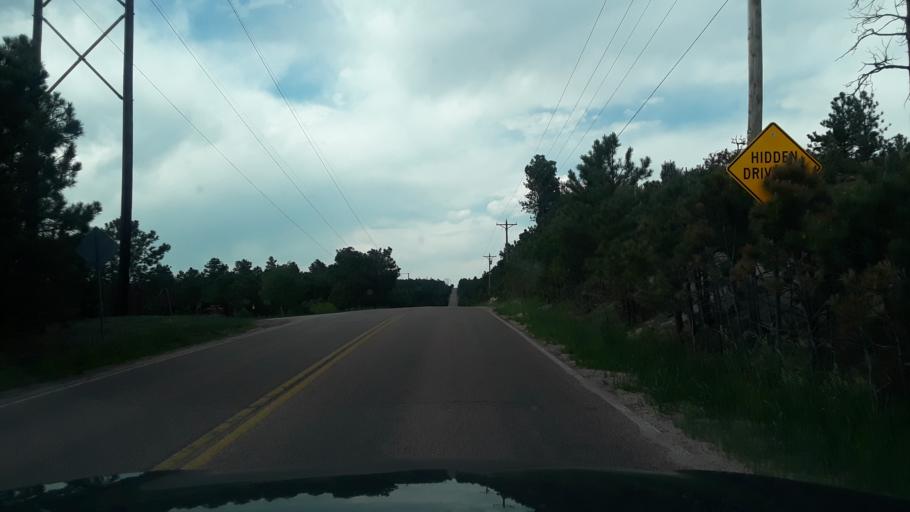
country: US
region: Colorado
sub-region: El Paso County
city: Gleneagle
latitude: 39.0587
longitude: -104.7849
